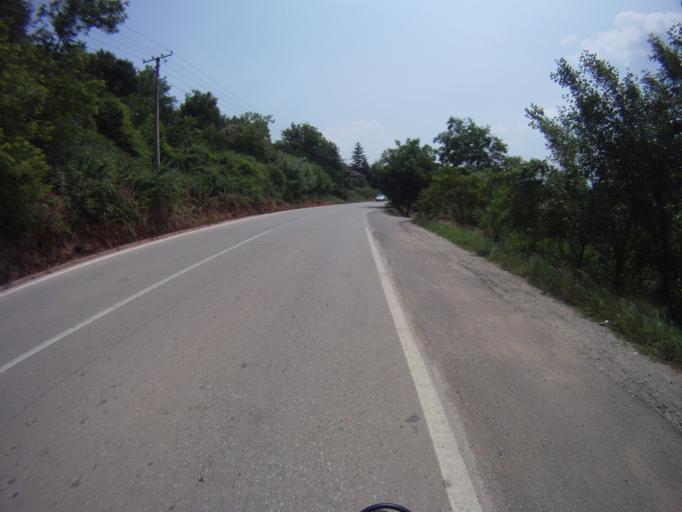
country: RS
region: Central Serbia
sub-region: Nisavski Okrug
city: Gadzin Han
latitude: 43.2376
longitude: 22.0199
